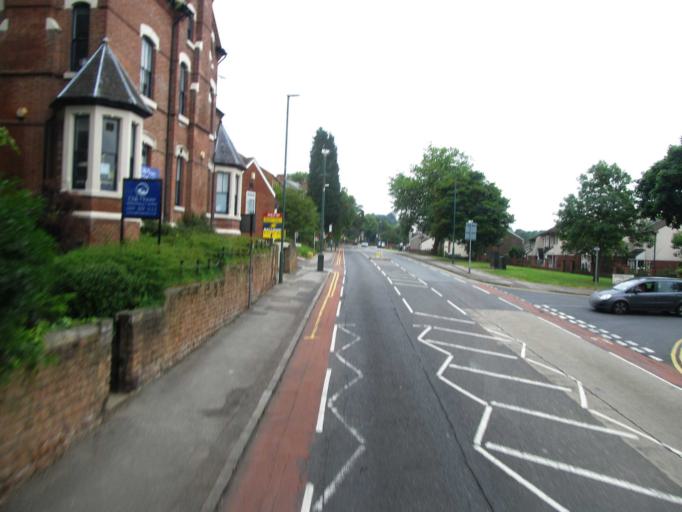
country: GB
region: England
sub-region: Nottingham
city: Nottingham
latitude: 52.9659
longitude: -1.1441
